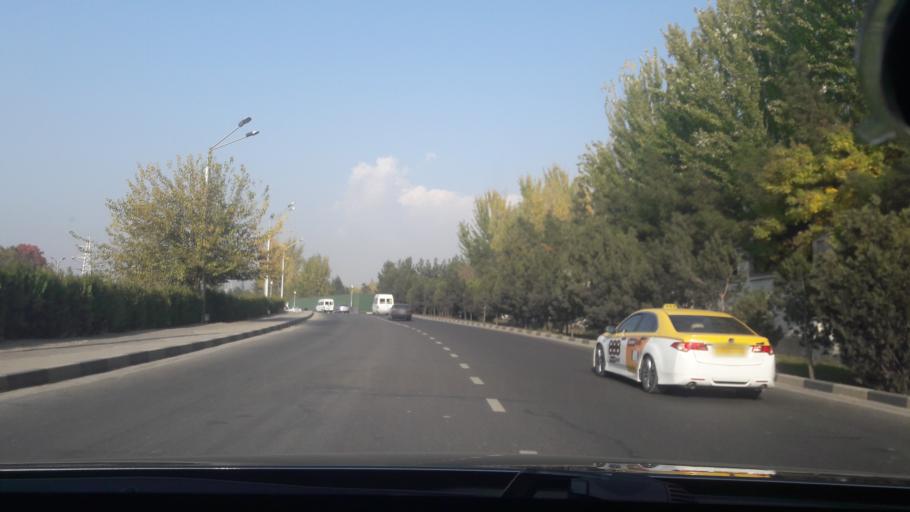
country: TJ
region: Dushanbe
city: Dushanbe
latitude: 38.5790
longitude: 68.7727
